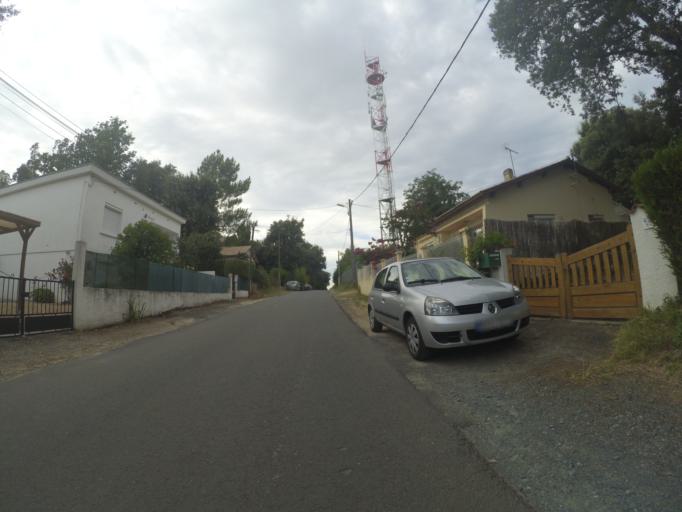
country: FR
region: Poitou-Charentes
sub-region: Departement de la Charente-Maritime
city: Meschers-sur-Gironde
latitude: 45.5666
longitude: -0.9622
